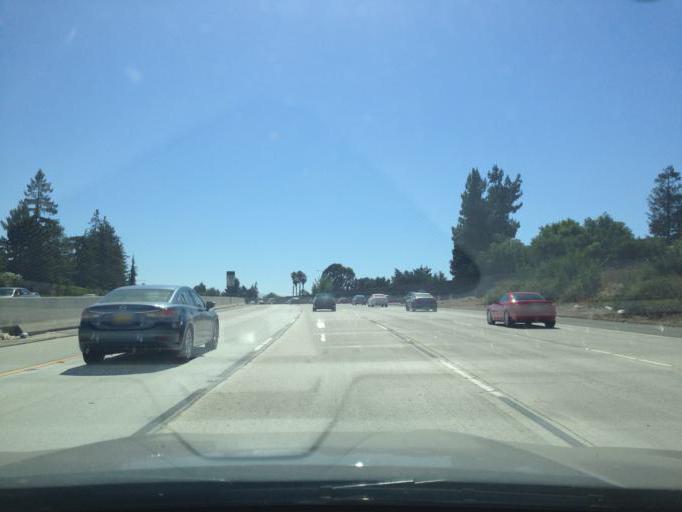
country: US
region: California
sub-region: Santa Clara County
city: Campbell
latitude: 37.3167
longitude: -121.9735
